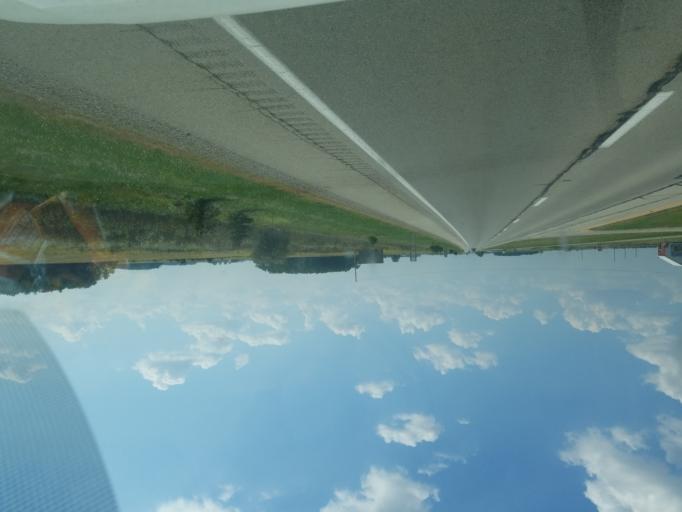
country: US
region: Indiana
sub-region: Allen County
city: Monroeville
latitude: 40.9845
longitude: -84.7757
